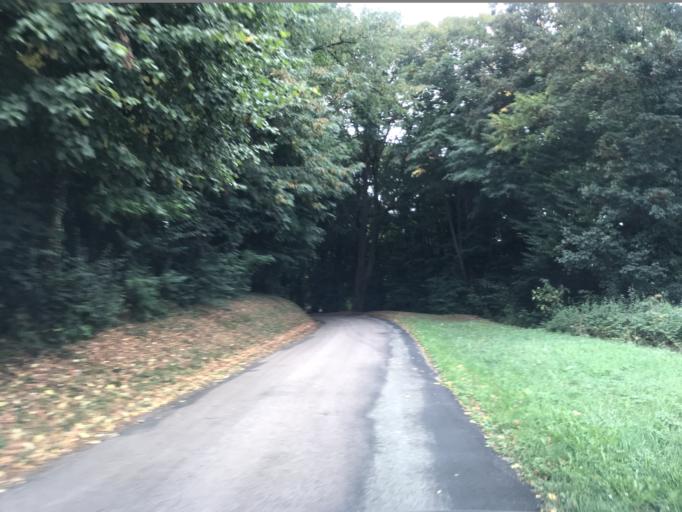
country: FR
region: Haute-Normandie
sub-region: Departement de l'Eure
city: Houlbec-Cocherel
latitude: 49.0634
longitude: 1.3360
